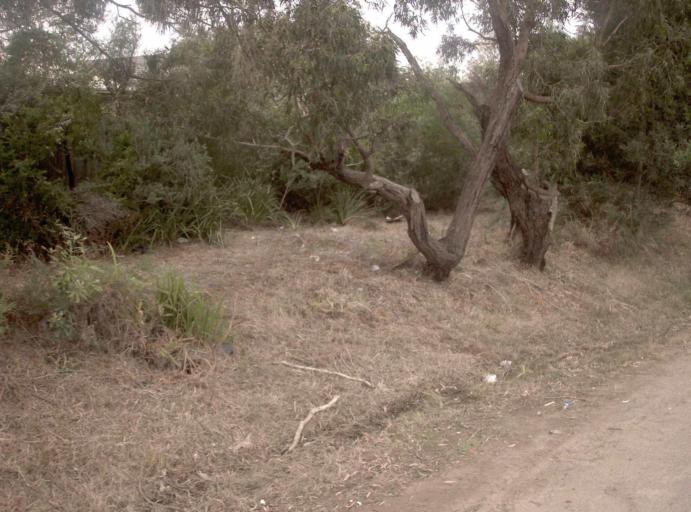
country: AU
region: Victoria
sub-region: Casey
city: Lynbrook
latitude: -38.0541
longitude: 145.2634
